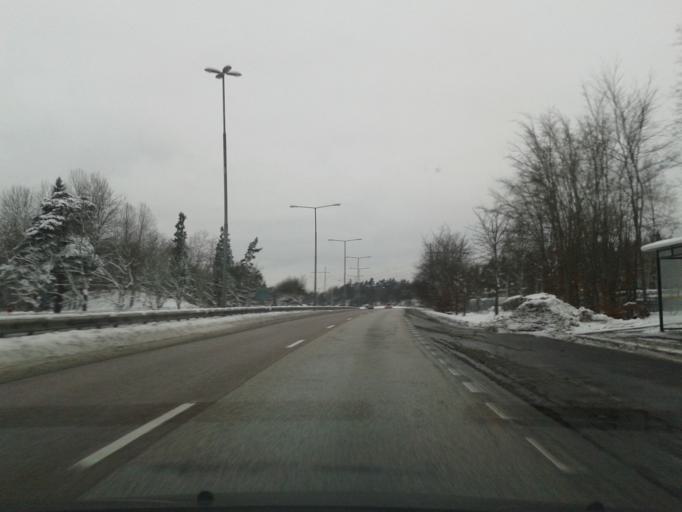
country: SE
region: Stockholm
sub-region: Stockholms Kommun
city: Arsta
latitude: 59.2635
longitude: 18.0639
